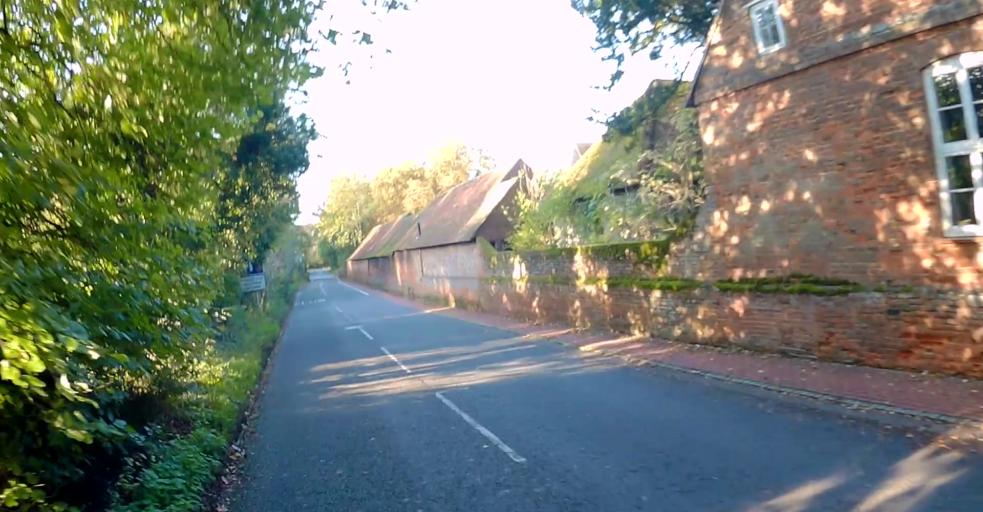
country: GB
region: England
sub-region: Hampshire
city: Old Basing
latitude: 51.2700
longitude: -1.0539
